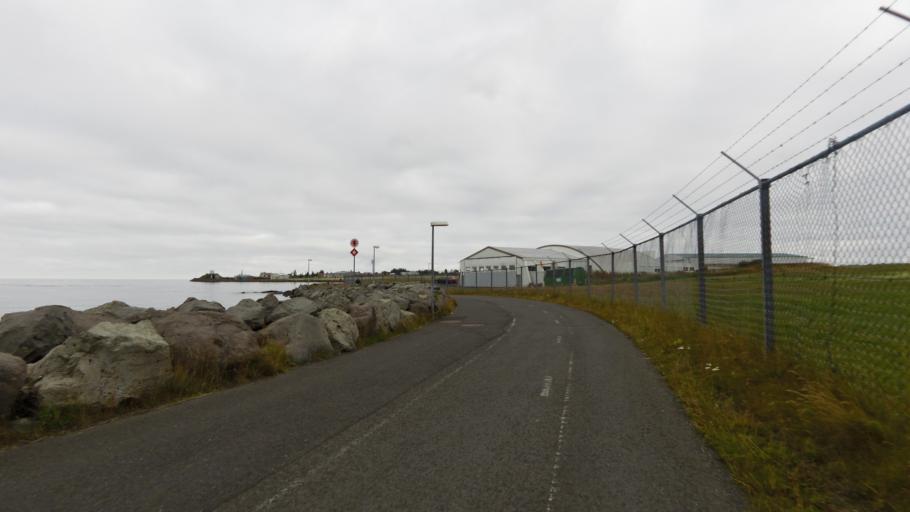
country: IS
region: Capital Region
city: Kopavogur
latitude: 64.1224
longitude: -21.9395
